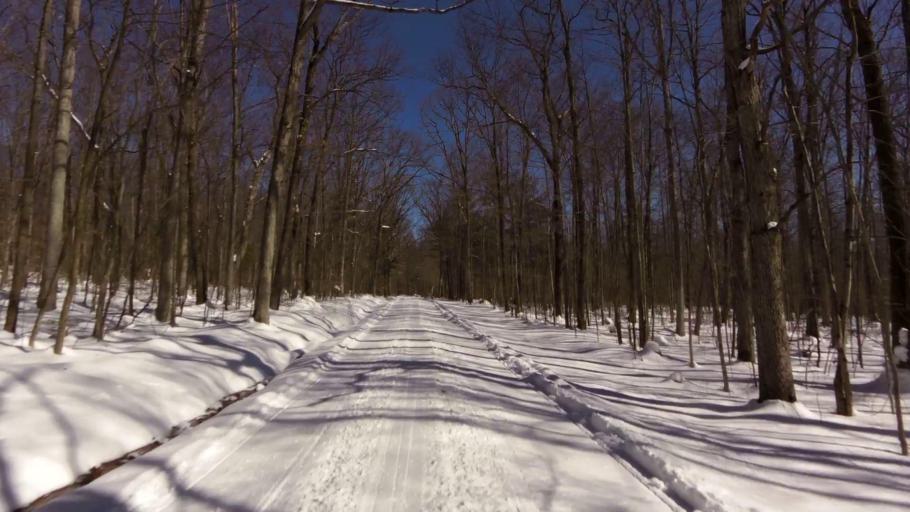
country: US
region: New York
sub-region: Allegany County
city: Houghton
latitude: 42.3487
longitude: -78.1958
